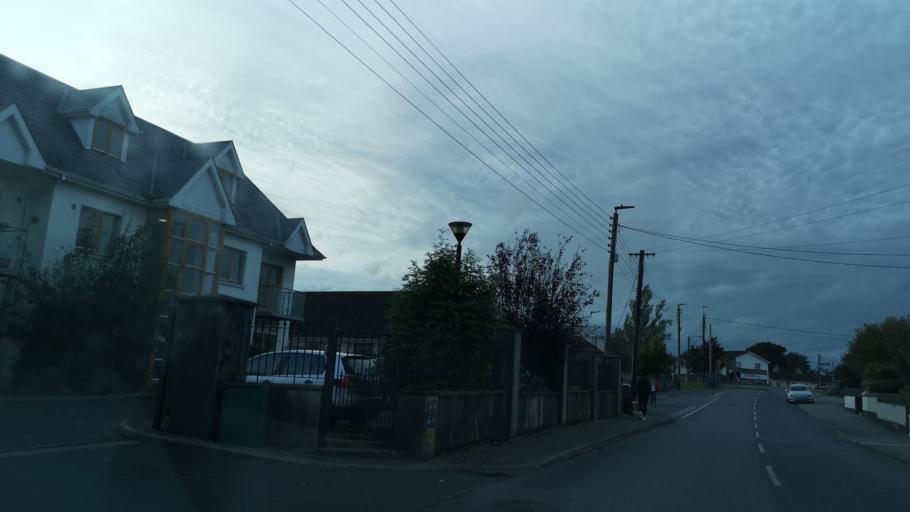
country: IE
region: Leinster
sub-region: An Iarmhi
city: Athlone
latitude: 53.4307
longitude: -7.9453
